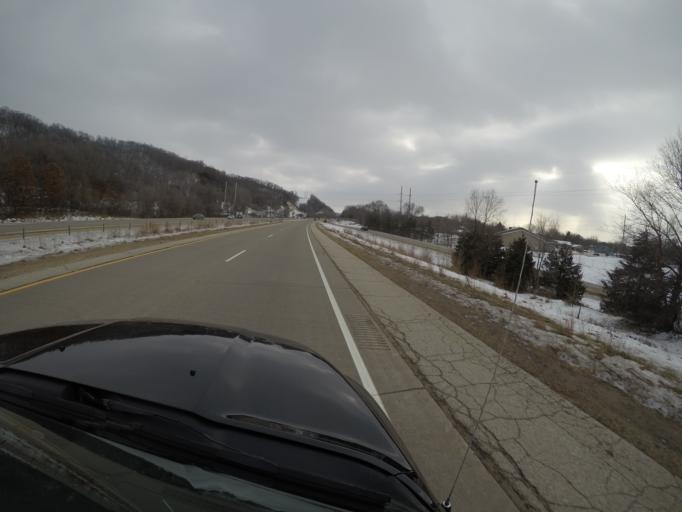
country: US
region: Wisconsin
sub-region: La Crosse County
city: Onalaska
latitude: 43.8963
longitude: -91.2187
